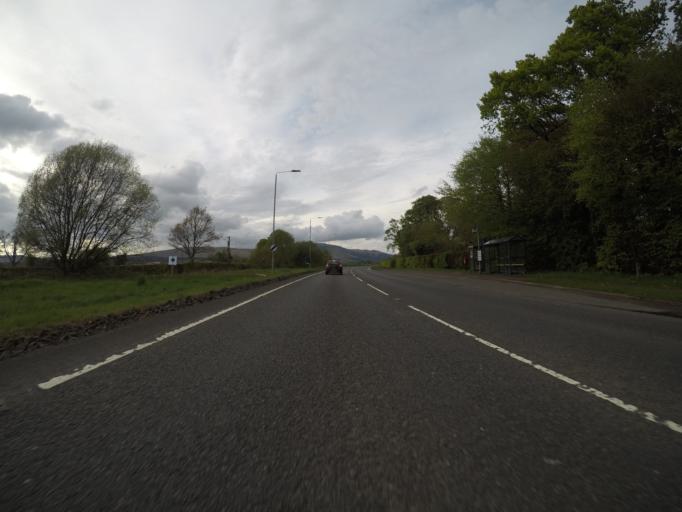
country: GB
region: Scotland
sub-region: West Dunbartonshire
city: Balloch
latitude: 56.0248
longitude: -4.6332
